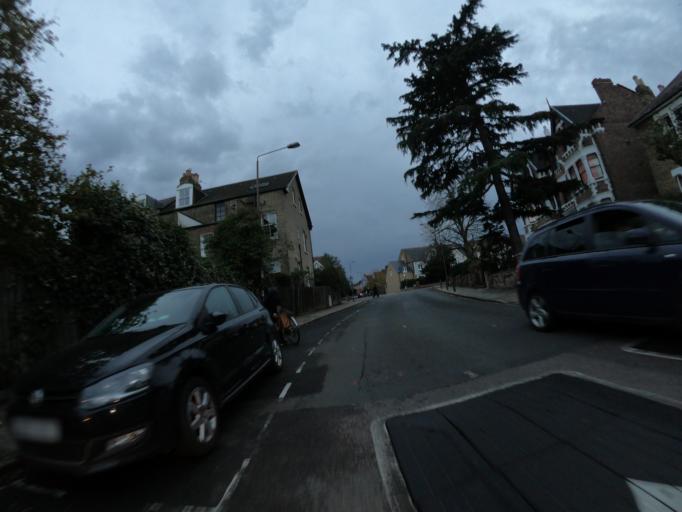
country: GB
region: England
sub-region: Greater London
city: Blackheath
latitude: 51.4803
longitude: 0.0083
